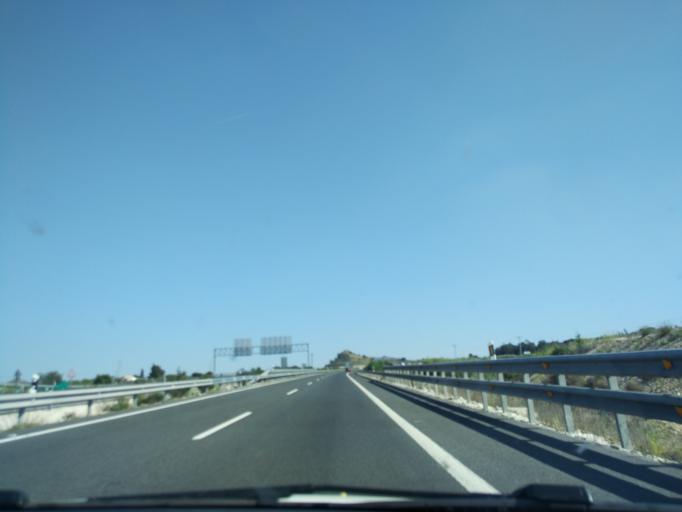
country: ES
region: Murcia
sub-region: Murcia
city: Ojos
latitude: 38.1857
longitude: -1.3231
